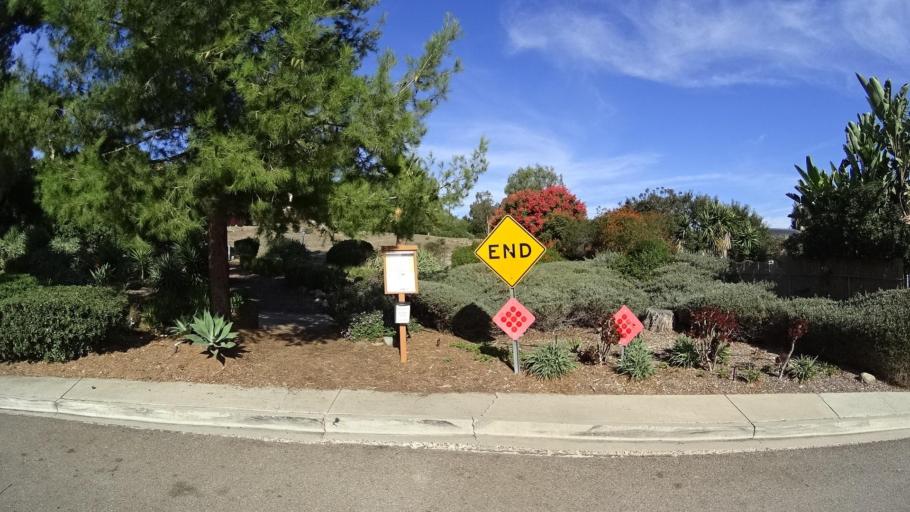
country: US
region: California
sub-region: San Diego County
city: Casa de Oro-Mount Helix
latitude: 32.7351
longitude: -116.9645
